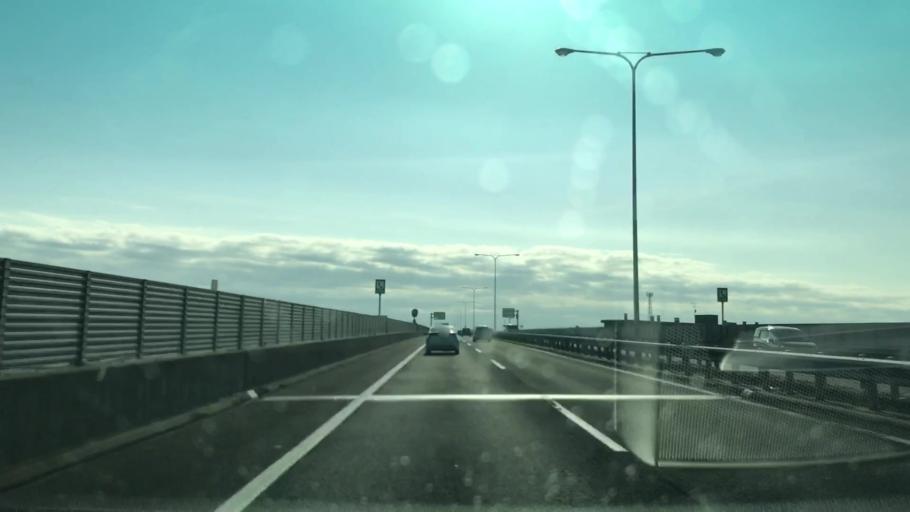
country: JP
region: Hokkaido
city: Sapporo
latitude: 43.0528
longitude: 141.4299
